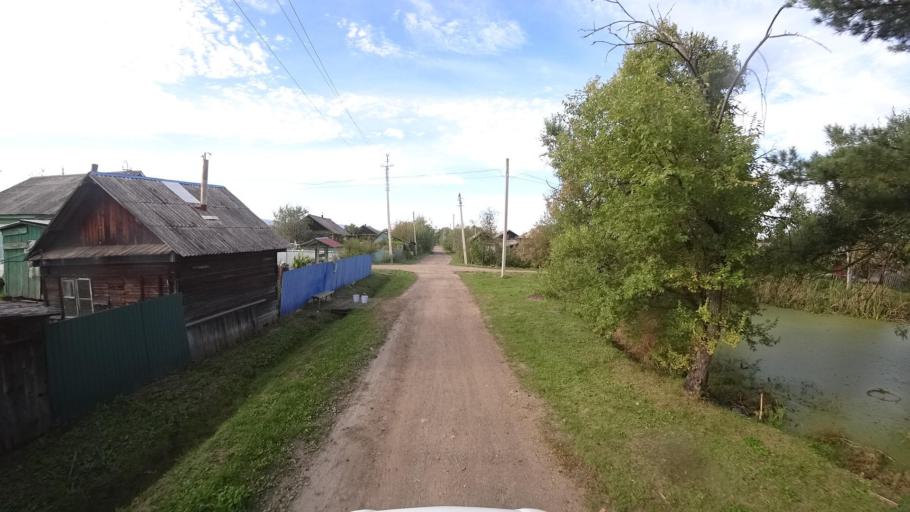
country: RU
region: Primorskiy
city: Dostoyevka
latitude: 44.2900
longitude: 133.4305
